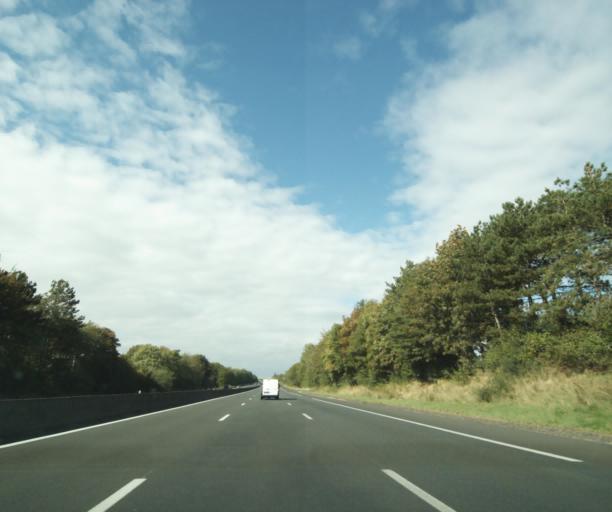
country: FR
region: Centre
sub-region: Departement d'Eure-et-Loir
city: Janville
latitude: 48.1700
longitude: 1.8538
